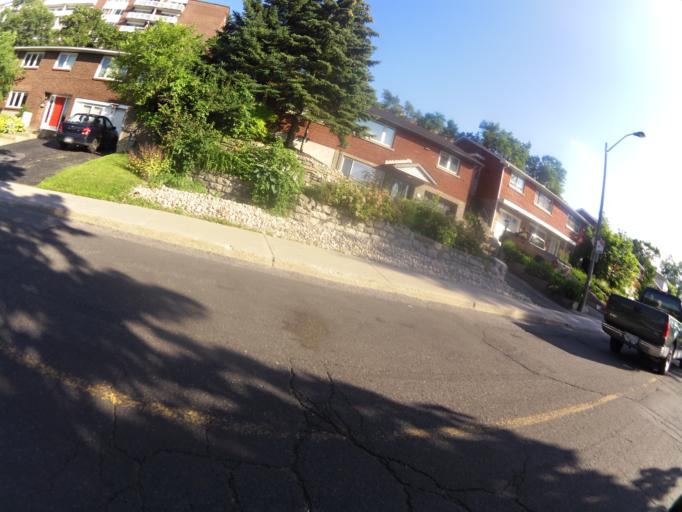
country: CA
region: Ontario
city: Ottawa
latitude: 45.3752
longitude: -75.7366
